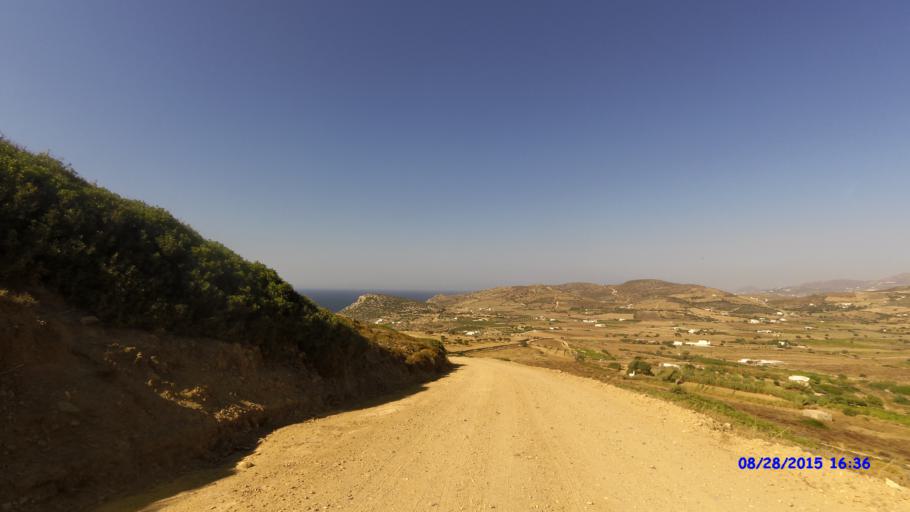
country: GR
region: South Aegean
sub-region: Nomos Kykladon
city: Antiparos
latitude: 37.0089
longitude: 25.0459
